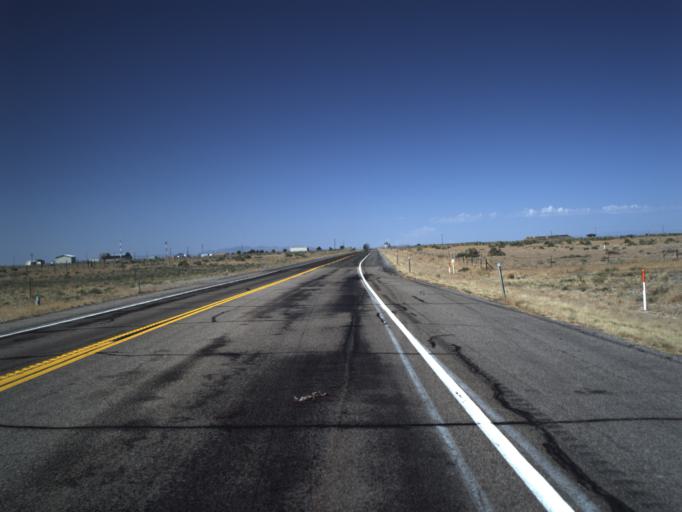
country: US
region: Utah
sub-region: Millard County
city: Delta
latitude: 39.3939
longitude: -112.5071
